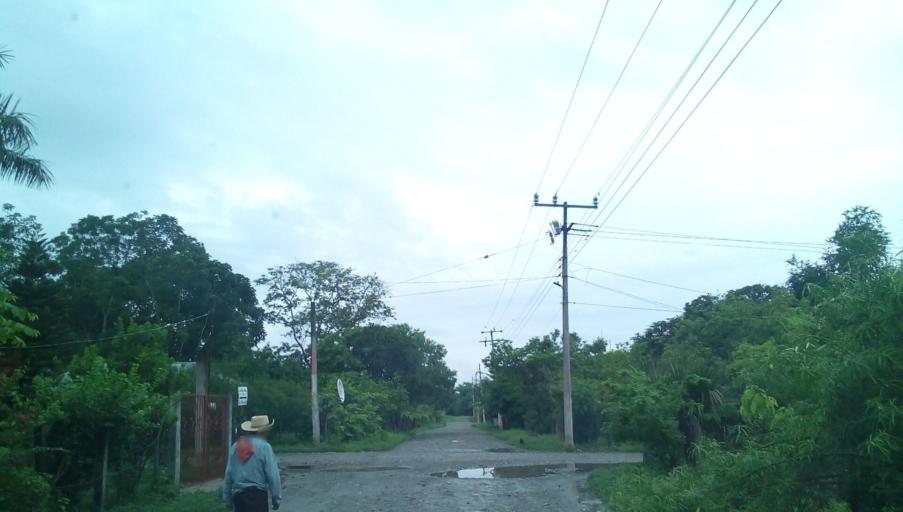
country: MX
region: Veracruz
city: Tempoal de Sanchez
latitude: 21.4192
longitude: -98.4256
